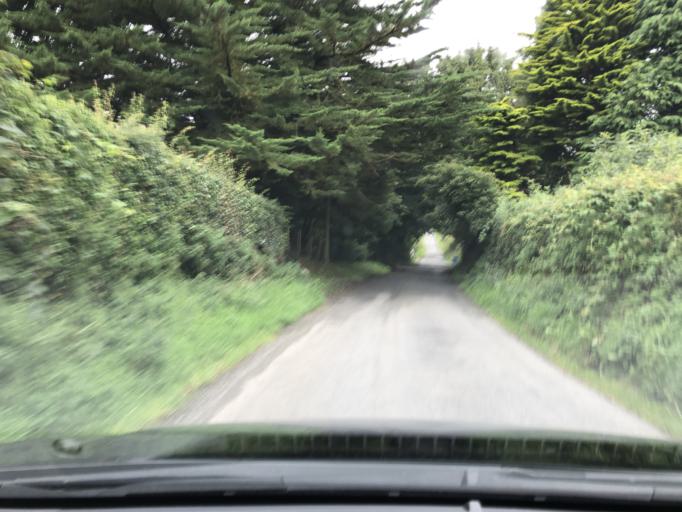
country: GB
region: Northern Ireland
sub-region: Down District
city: Dundrum
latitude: 54.3009
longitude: -5.8545
